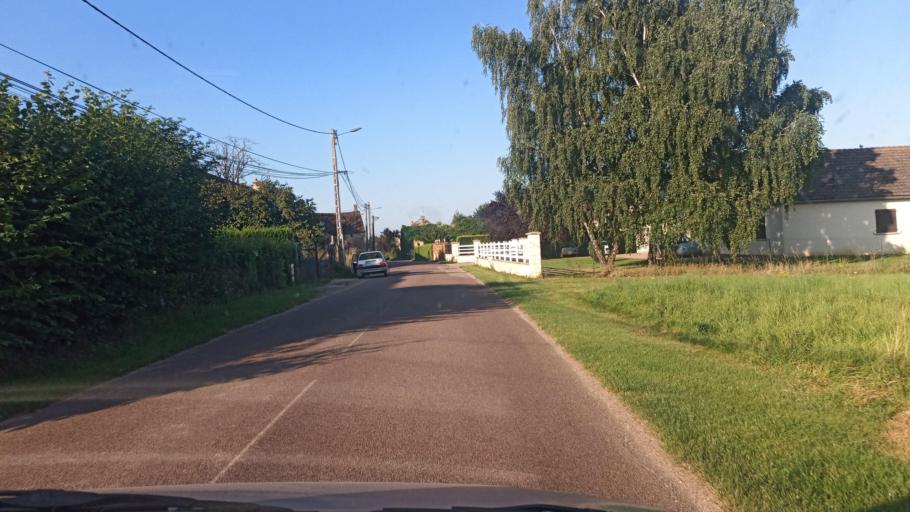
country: FR
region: Bourgogne
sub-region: Departement de l'Yonne
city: Saint-Valerien
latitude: 48.1932
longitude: 3.1203
